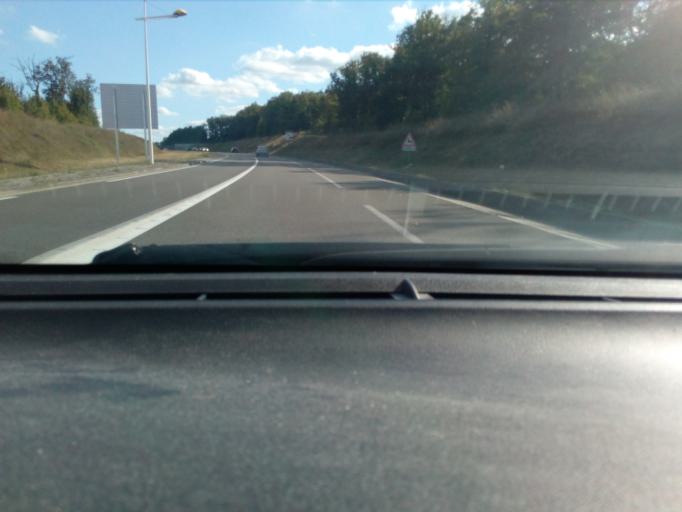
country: FR
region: Poitou-Charentes
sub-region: Departement de la Charente
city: Soyaux
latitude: 45.6496
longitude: 0.2079
